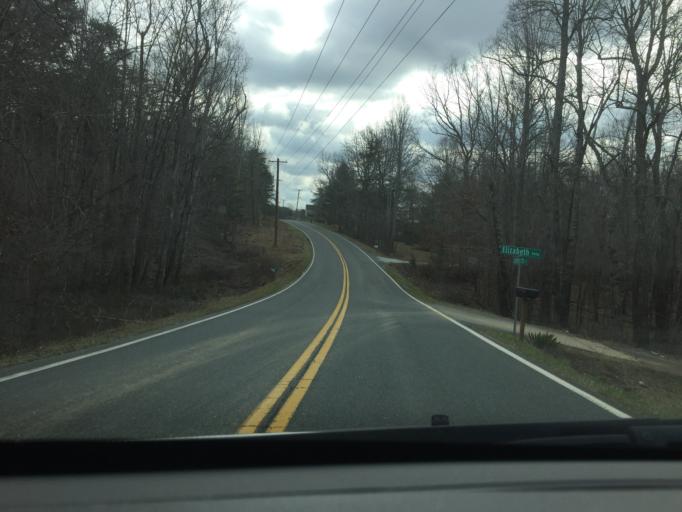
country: US
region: Virginia
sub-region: City of Lynchburg
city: West Lynchburg
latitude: 37.3308
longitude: -79.1668
